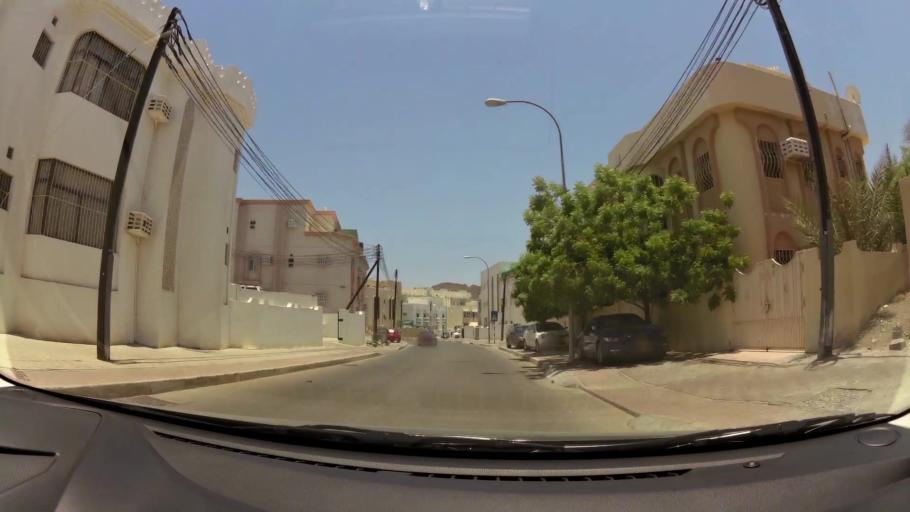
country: OM
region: Muhafazat Masqat
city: Muscat
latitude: 23.6145
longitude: 58.5371
